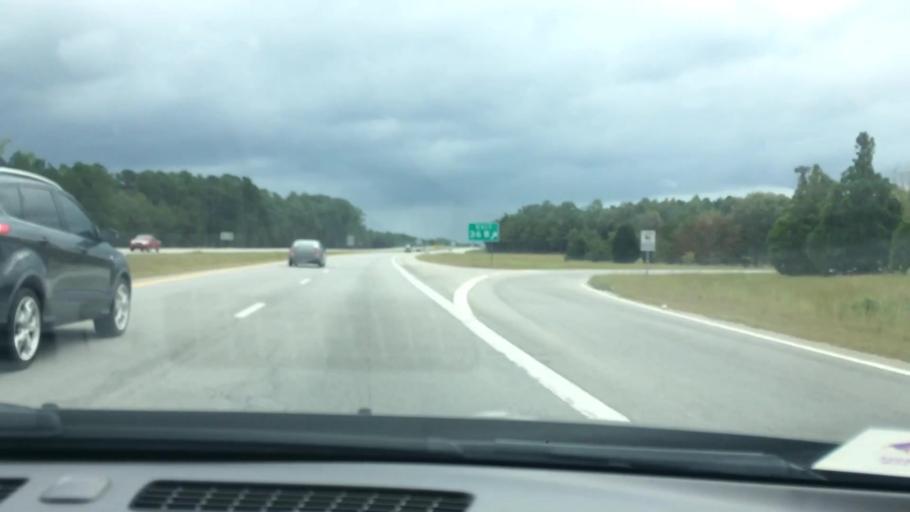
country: US
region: North Carolina
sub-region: Wilson County
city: Lucama
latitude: 35.7609
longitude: -78.0279
